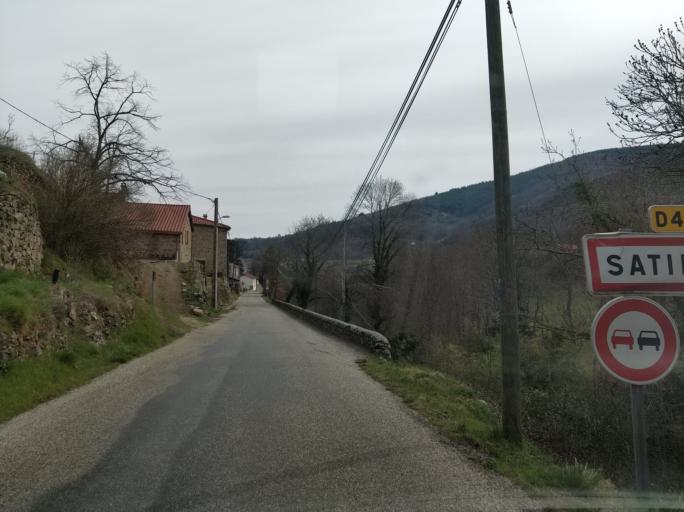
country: FR
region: Rhone-Alpes
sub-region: Departement de l'Ardeche
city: Satillieu
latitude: 45.1521
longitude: 4.6080
